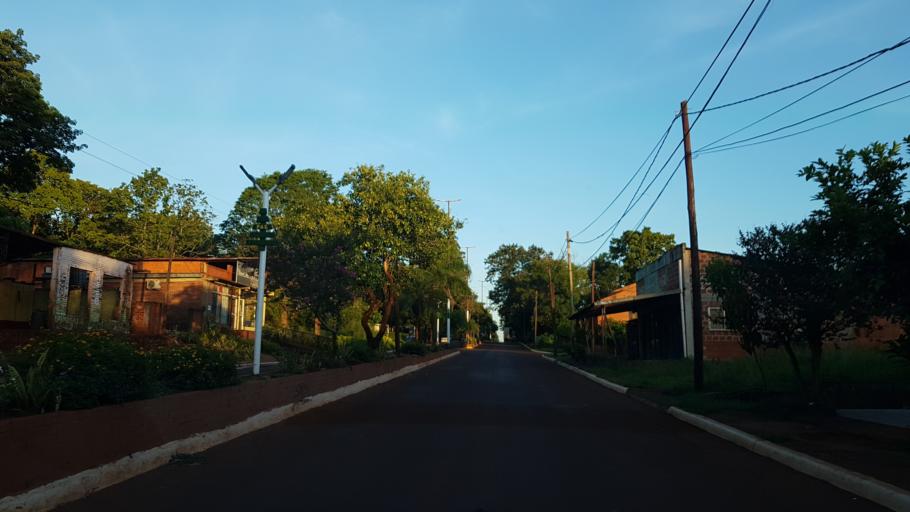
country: AR
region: Misiones
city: Puerto Libertad
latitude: -25.9209
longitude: -54.5792
